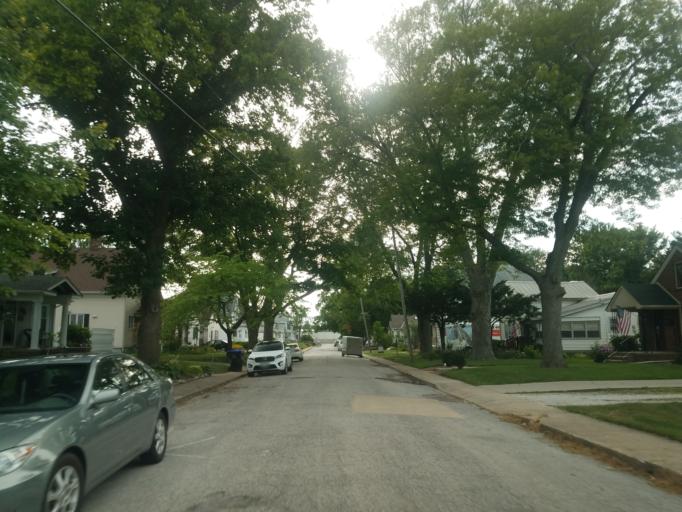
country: US
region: Illinois
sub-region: McLean County
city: Bloomington
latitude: 40.4790
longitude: -88.9771
